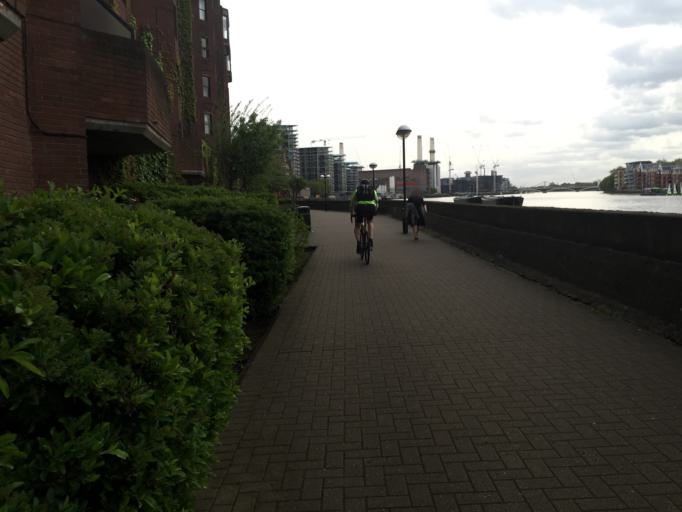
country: GB
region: England
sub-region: Greater London
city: City of Westminster
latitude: 51.4845
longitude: -0.1301
